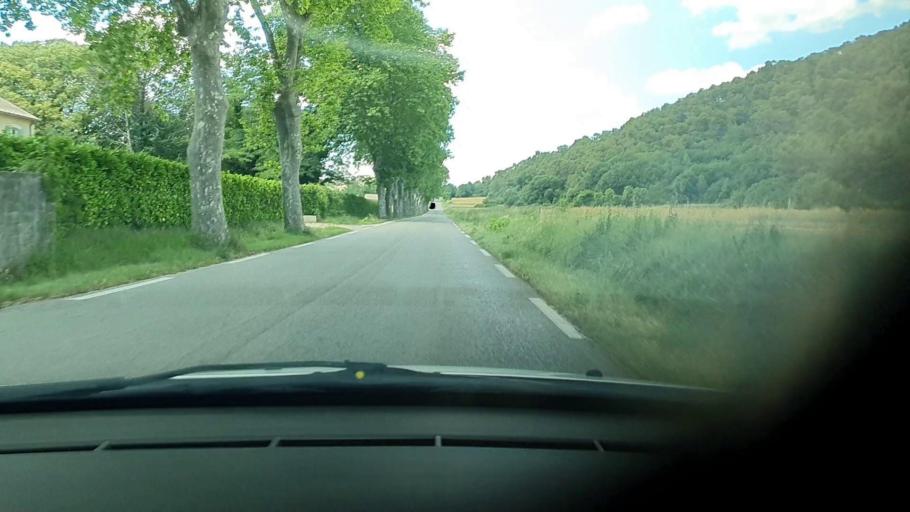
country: FR
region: Languedoc-Roussillon
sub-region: Departement du Gard
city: Montaren-et-Saint-Mediers
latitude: 44.0317
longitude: 4.3709
